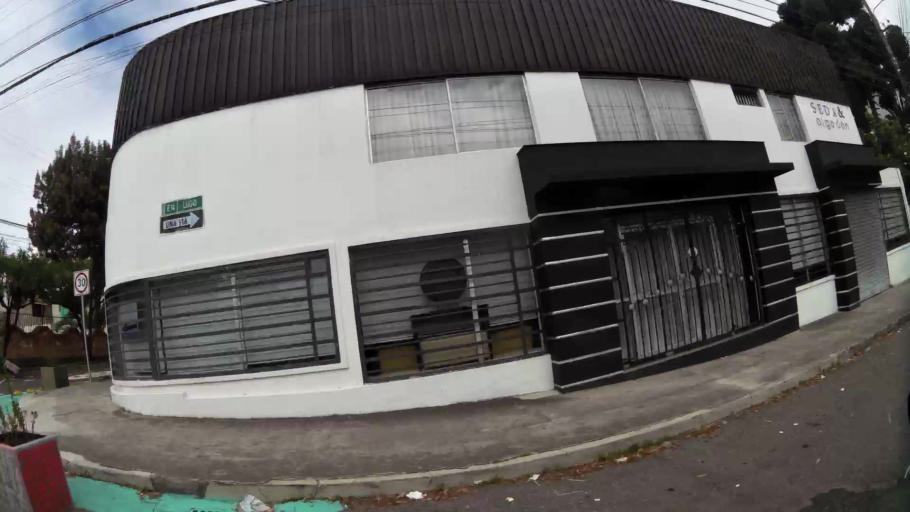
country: EC
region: Pichincha
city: Quito
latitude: -0.2095
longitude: -78.4836
